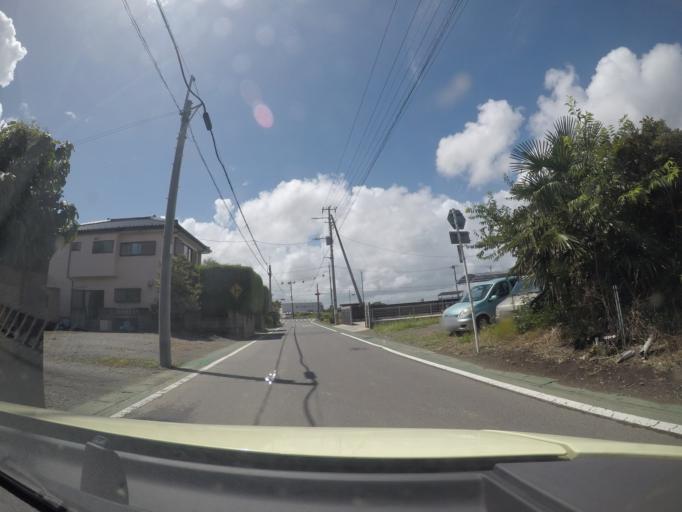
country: JP
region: Ibaraki
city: Mitsukaido
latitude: 36.0658
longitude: 140.0036
